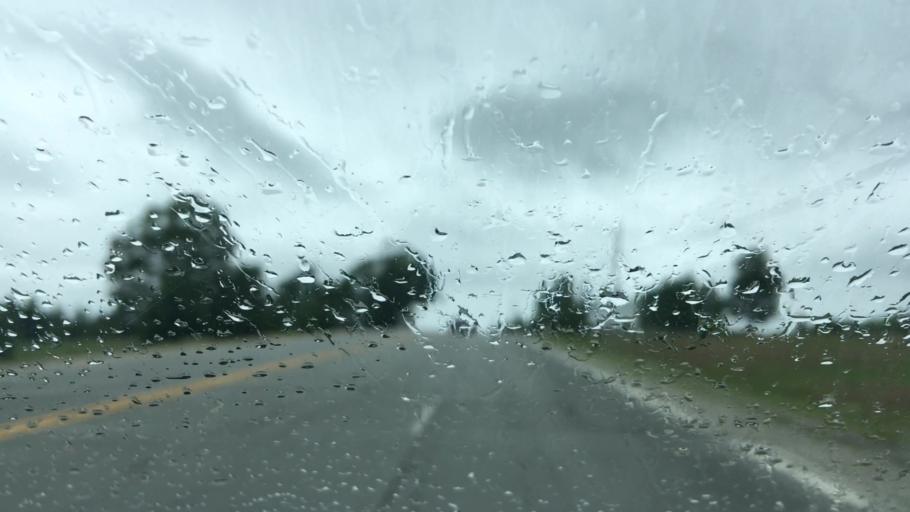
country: US
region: Maine
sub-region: Washington County
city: Cherryfield
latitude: 44.8470
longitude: -68.0629
